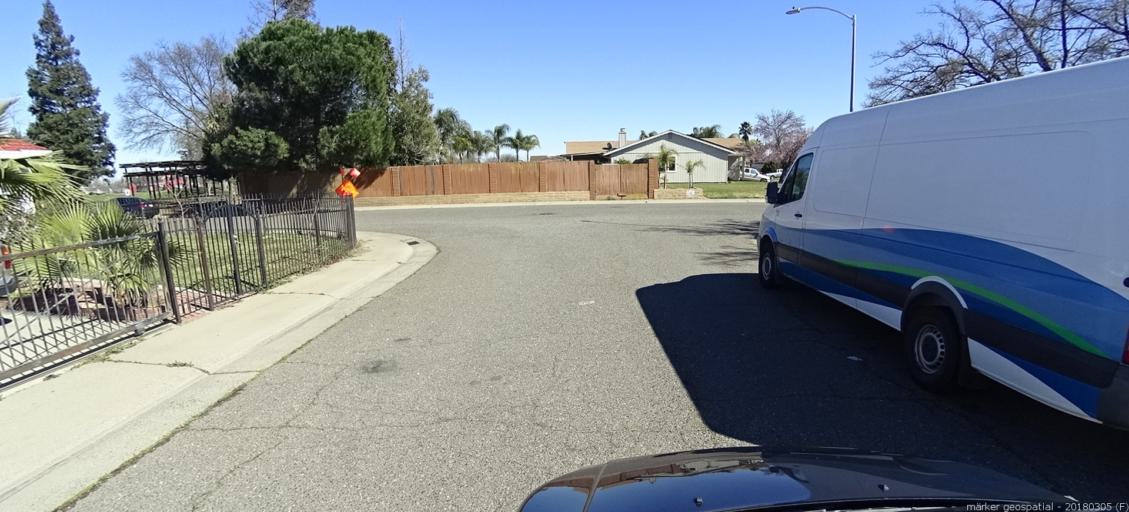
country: US
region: California
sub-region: Sacramento County
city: Florin
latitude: 38.4915
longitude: -121.3829
